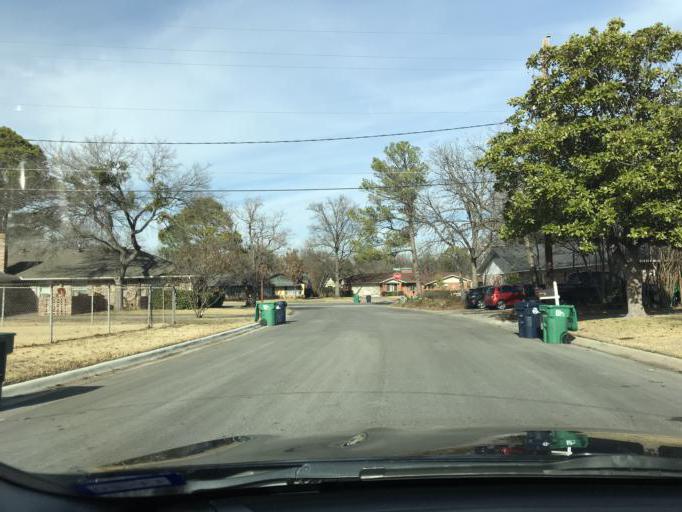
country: US
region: Texas
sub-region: Denton County
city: Denton
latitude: 33.2327
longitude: -97.1472
